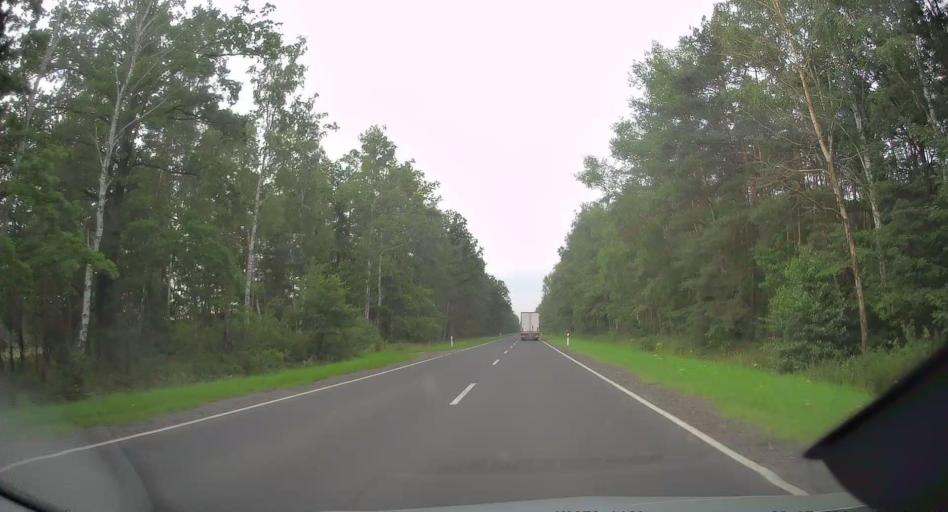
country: PL
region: Lodz Voivodeship
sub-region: Powiat radomszczanski
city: Plawno
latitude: 50.9785
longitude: 19.4104
